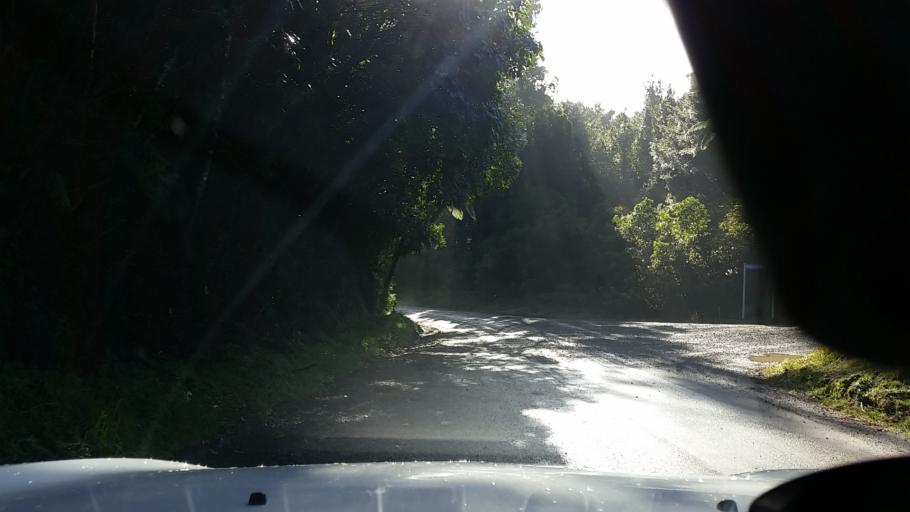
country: NZ
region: Bay of Plenty
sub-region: Kawerau District
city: Kawerau
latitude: -37.9891
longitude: 176.5035
